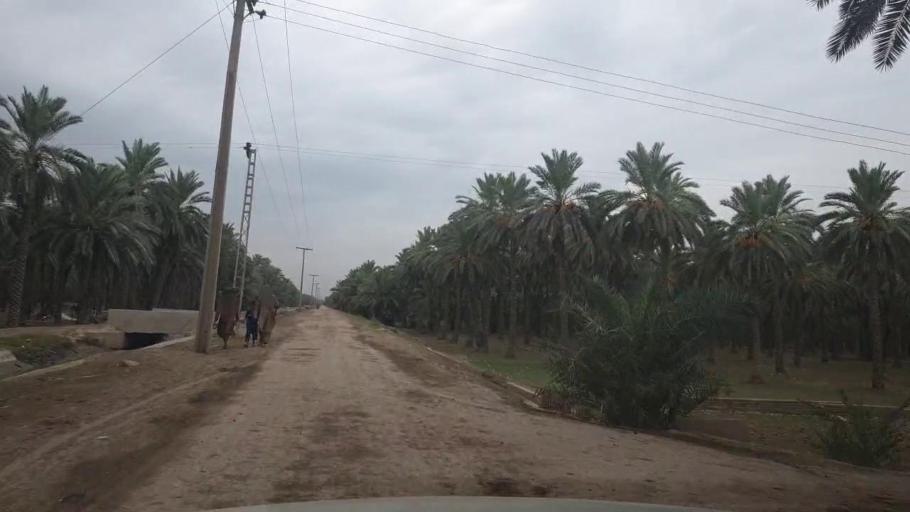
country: PK
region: Sindh
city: Sukkur
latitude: 27.6140
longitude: 68.8180
